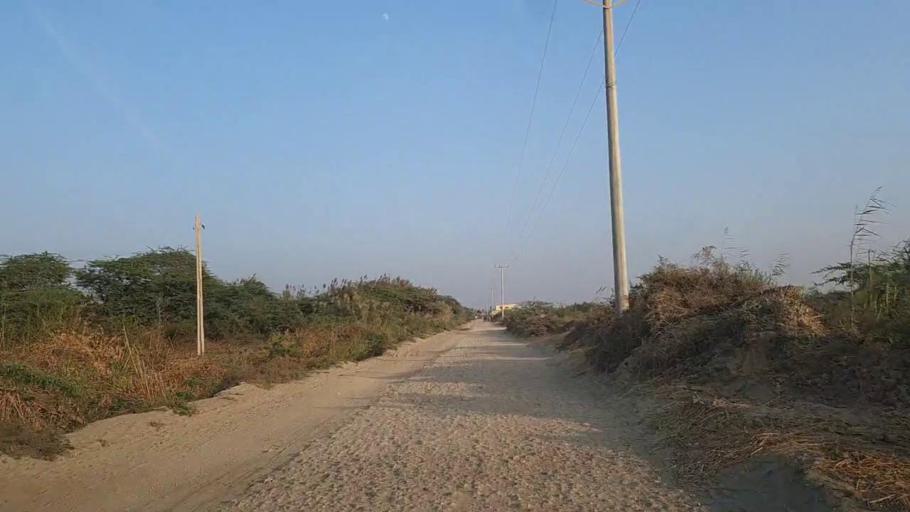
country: PK
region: Sindh
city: Keti Bandar
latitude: 24.2748
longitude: 67.6691
